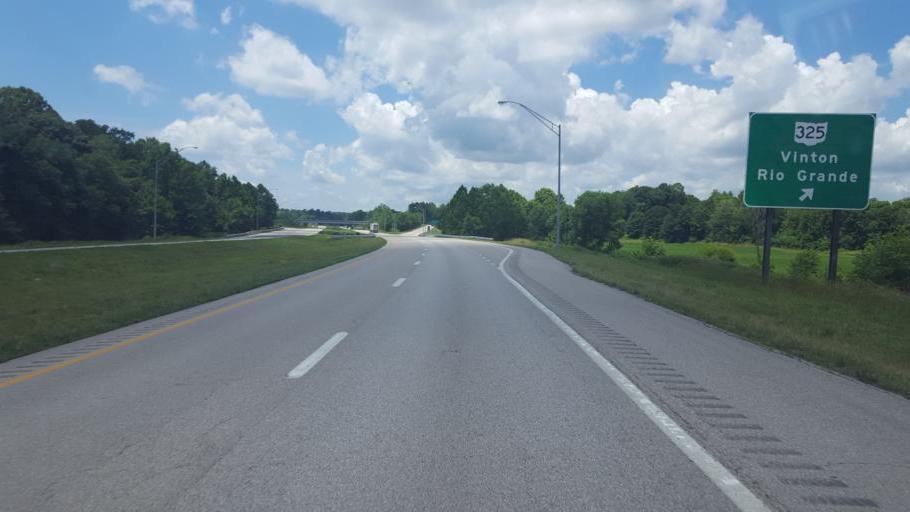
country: US
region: Ohio
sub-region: Gallia County
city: Gallipolis
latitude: 38.8937
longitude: -82.3765
